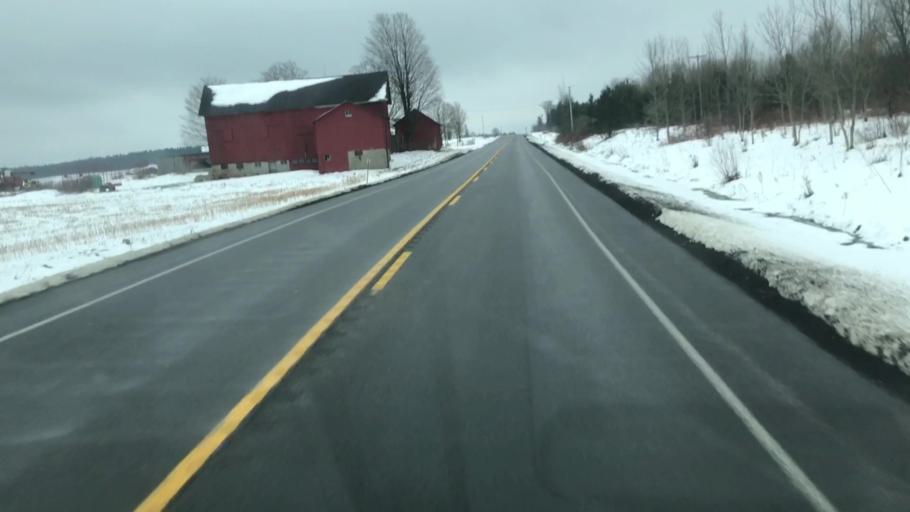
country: US
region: New York
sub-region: Cayuga County
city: Moravia
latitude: 42.7684
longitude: -76.3319
